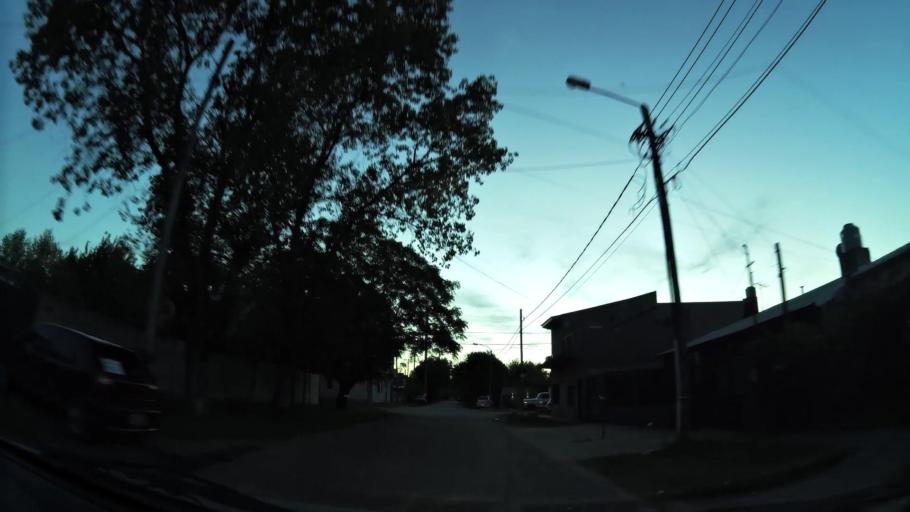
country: AR
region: Buenos Aires
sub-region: Partido de Quilmes
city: Quilmes
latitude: -34.7781
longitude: -58.2195
